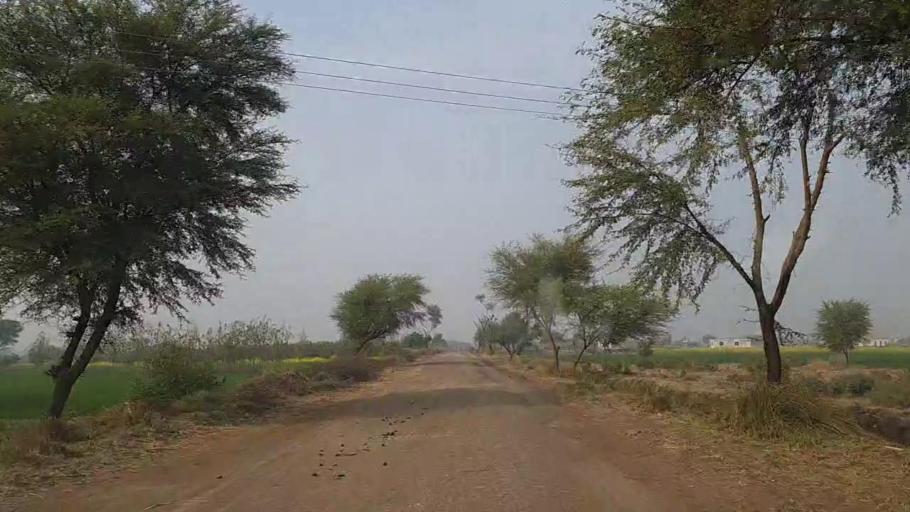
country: PK
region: Sindh
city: Sanghar
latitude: 26.1003
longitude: 68.8961
